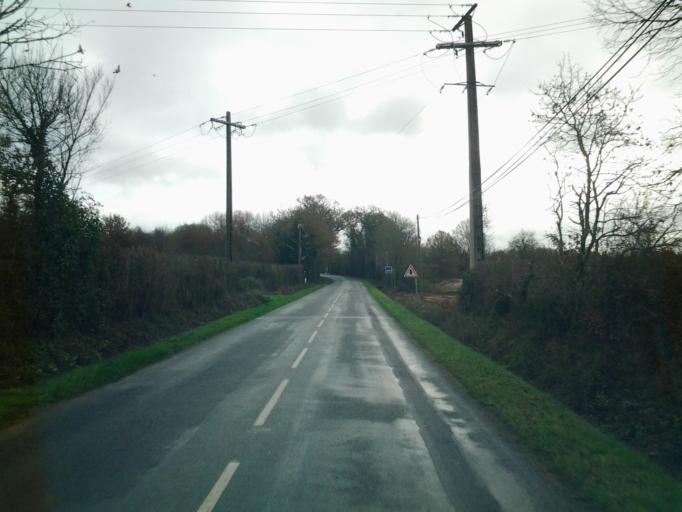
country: FR
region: Pays de la Loire
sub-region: Departement de la Vendee
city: La Roche-sur-Yon
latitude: 46.6557
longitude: -1.3923
